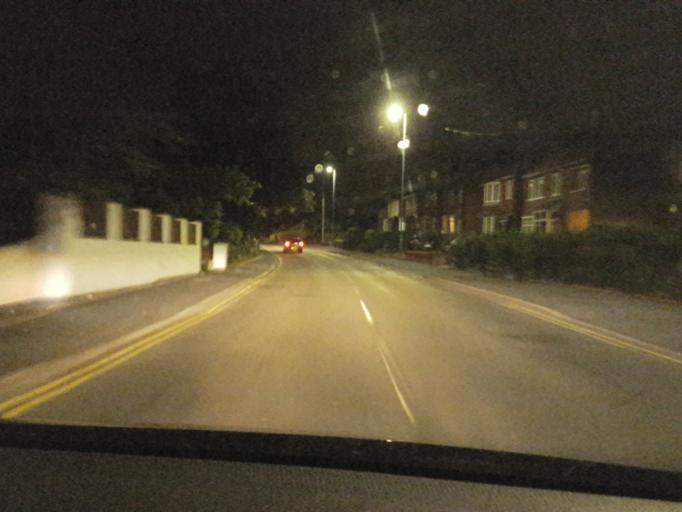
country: GB
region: England
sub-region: Leicestershire
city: Loughborough
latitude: 52.7623
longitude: -1.2241
